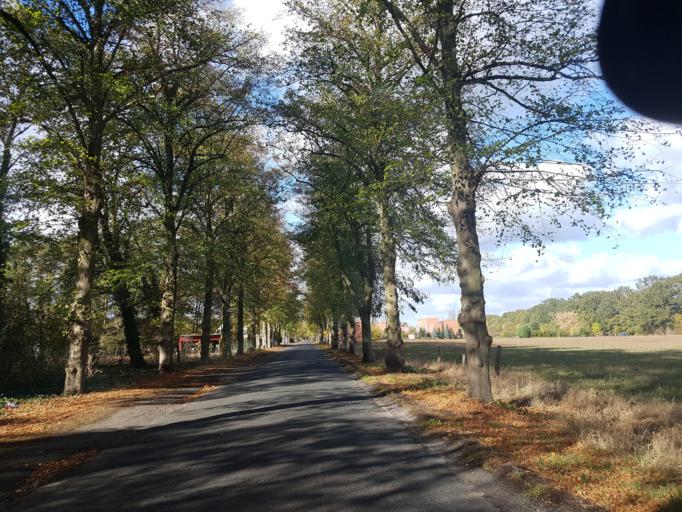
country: DE
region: Brandenburg
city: Nauen
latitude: 52.6607
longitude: 12.9167
